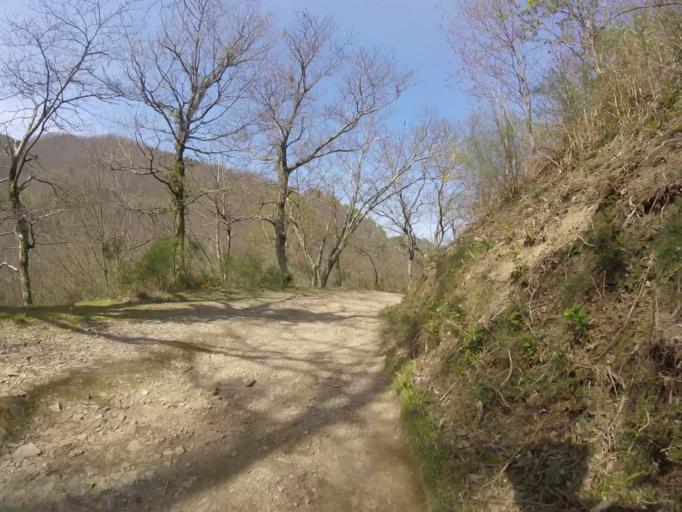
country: ES
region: Basque Country
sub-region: Provincia de Guipuzcoa
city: Irun
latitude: 43.2670
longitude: -1.8096
